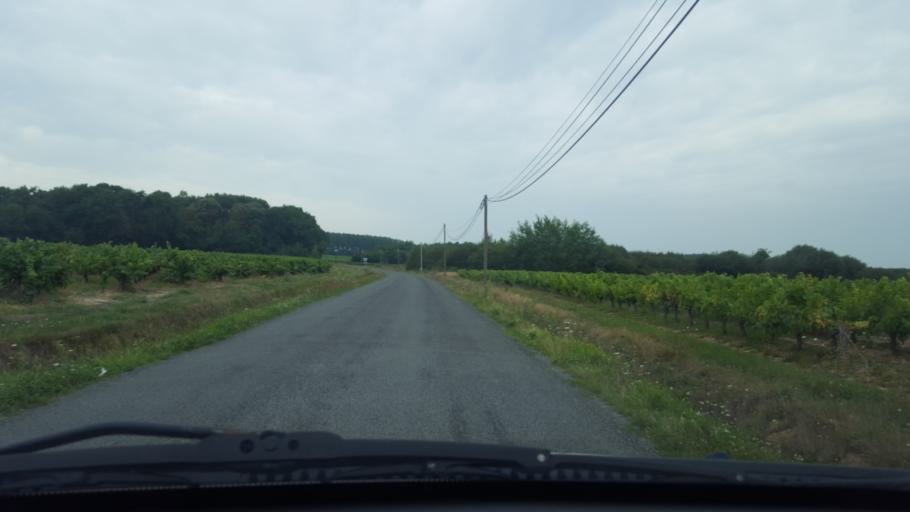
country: FR
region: Pays de la Loire
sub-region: Departement de la Loire-Atlantique
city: Saint-Philbert-de-Grand-Lieu
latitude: 47.0197
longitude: -1.6308
